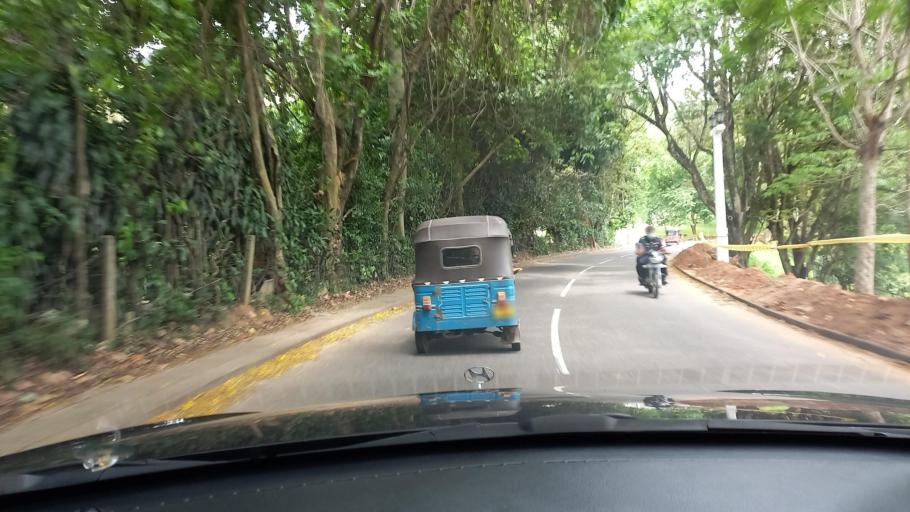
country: LK
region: Central
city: Kandy
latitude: 7.2620
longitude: 80.5995
